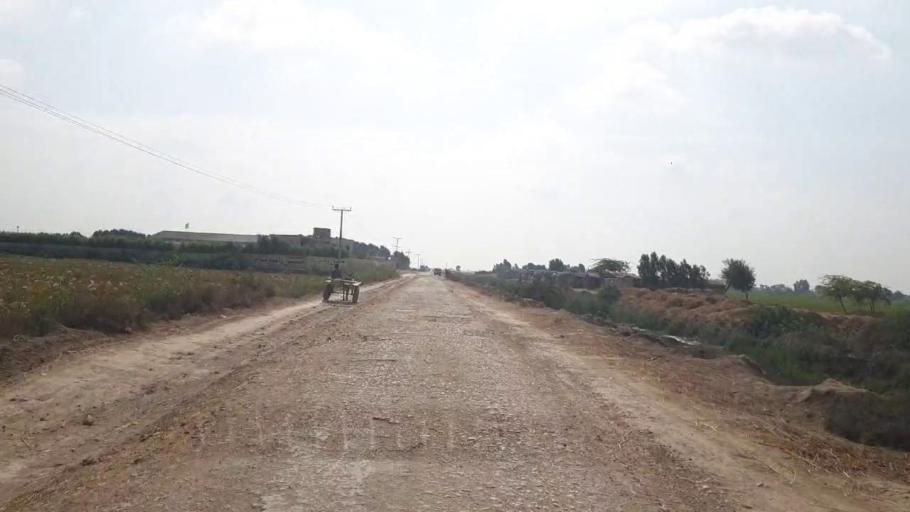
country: PK
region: Sindh
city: Kario
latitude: 24.6383
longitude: 68.5467
